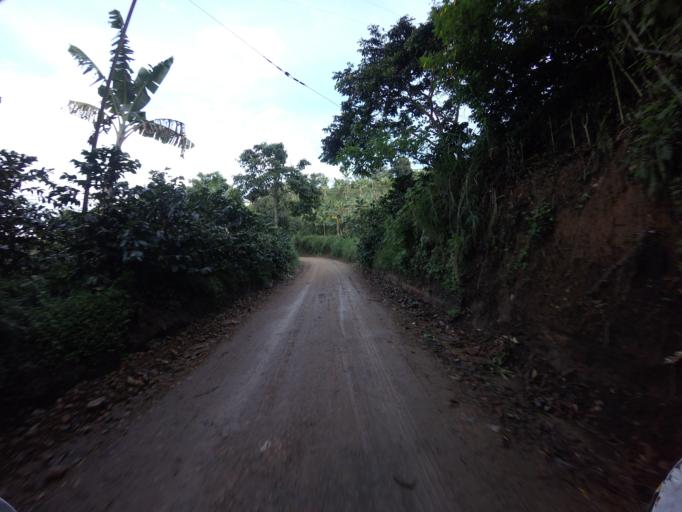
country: CO
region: Valle del Cauca
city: Ulloa
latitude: 4.7077
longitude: -75.7087
